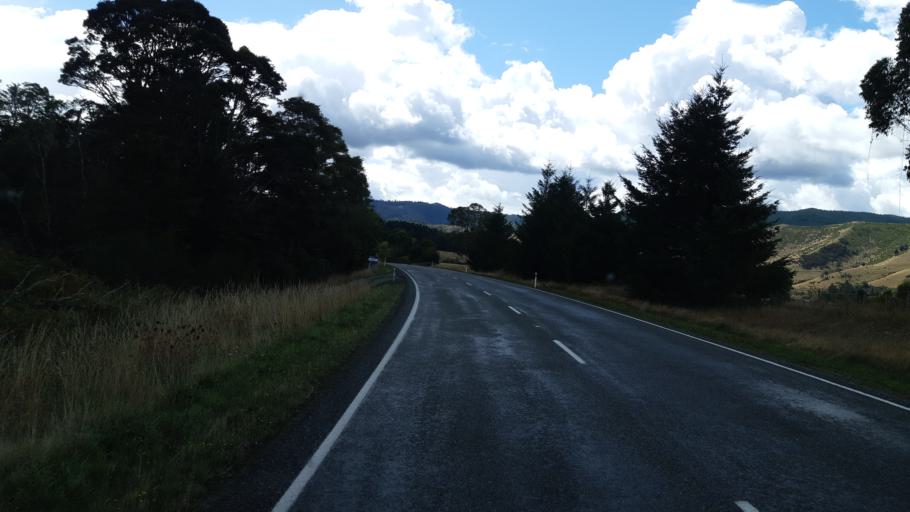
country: NZ
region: Tasman
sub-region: Tasman District
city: Wakefield
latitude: -41.5614
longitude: 172.7810
